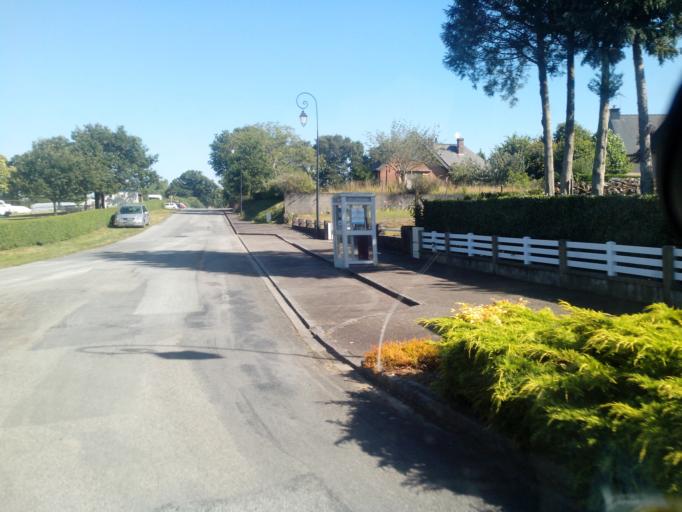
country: FR
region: Brittany
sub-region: Departement d'Ille-et-Vilaine
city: Paimpont
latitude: 48.0141
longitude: -2.1708
